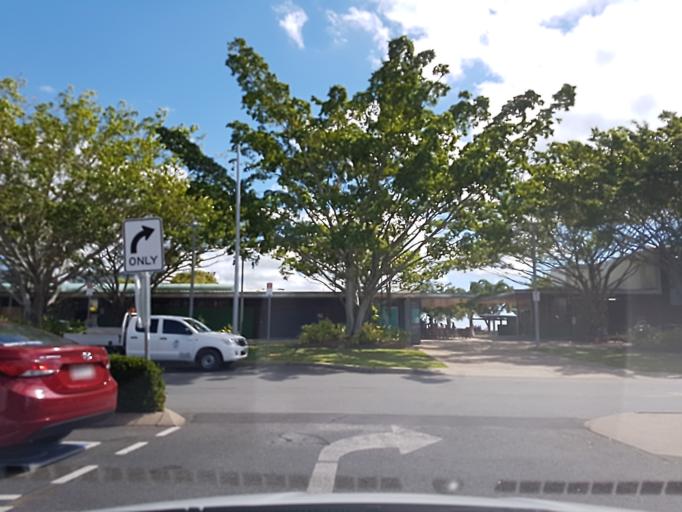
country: AU
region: Queensland
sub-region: Cairns
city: Cairns
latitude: -16.9201
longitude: 145.7788
